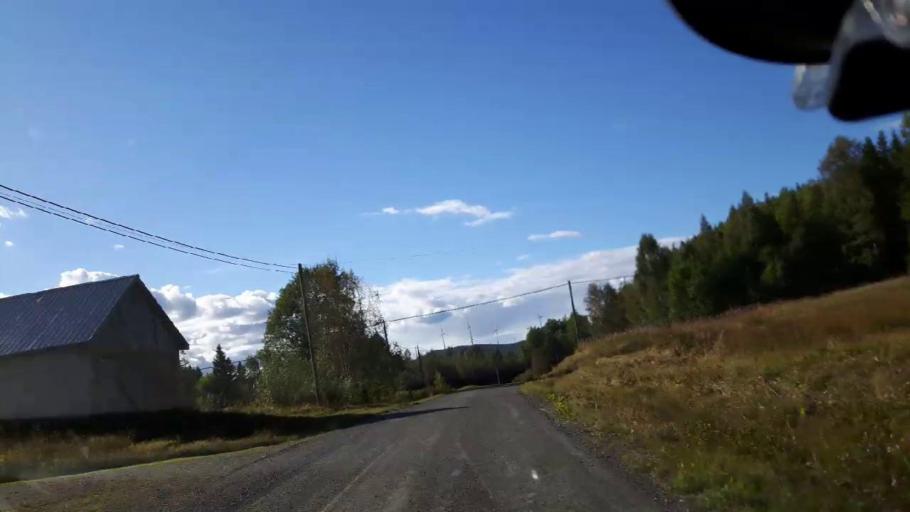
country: SE
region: Jaemtland
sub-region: Ragunda Kommun
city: Hammarstrand
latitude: 63.4919
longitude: 16.0454
